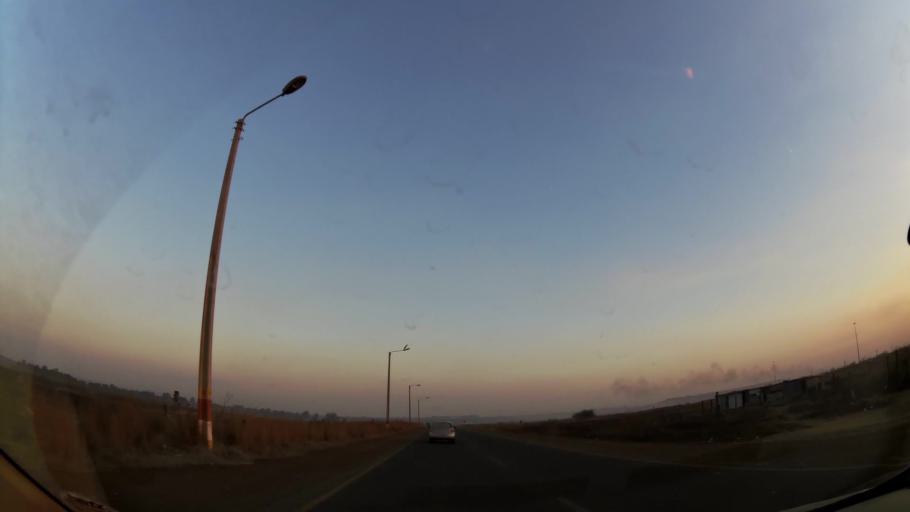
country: ZA
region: Gauteng
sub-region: Ekurhuleni Metropolitan Municipality
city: Springs
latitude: -26.3194
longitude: 28.4250
